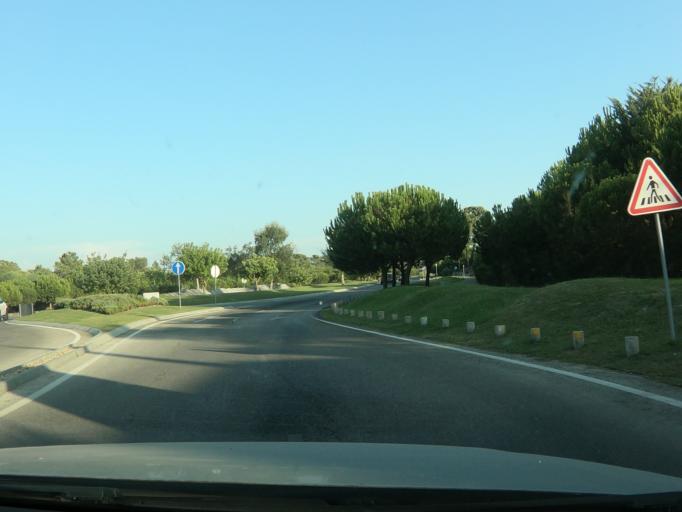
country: PT
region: Setubal
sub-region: Setubal
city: Setubal
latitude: 38.4880
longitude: -8.8976
